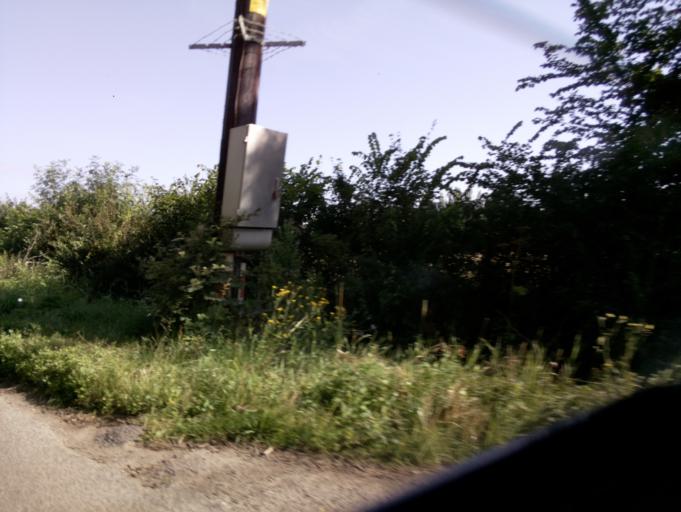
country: GB
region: England
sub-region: Oxfordshire
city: Bampton
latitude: 51.7150
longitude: -1.5264
